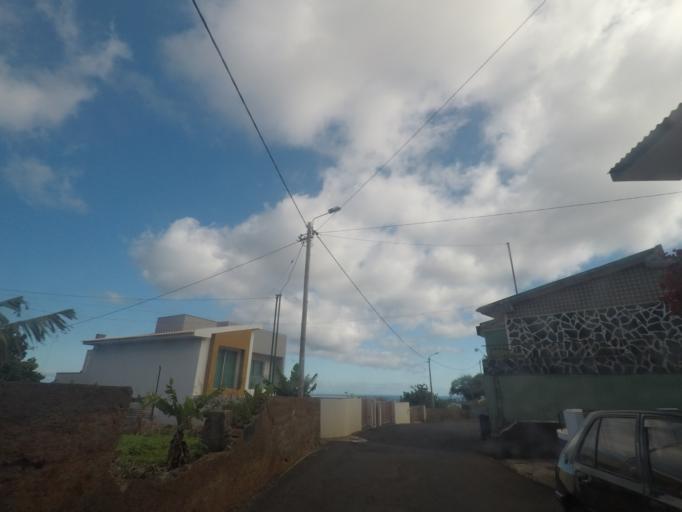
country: PT
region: Madeira
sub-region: Machico
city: Machico
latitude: 32.6999
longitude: -16.7754
